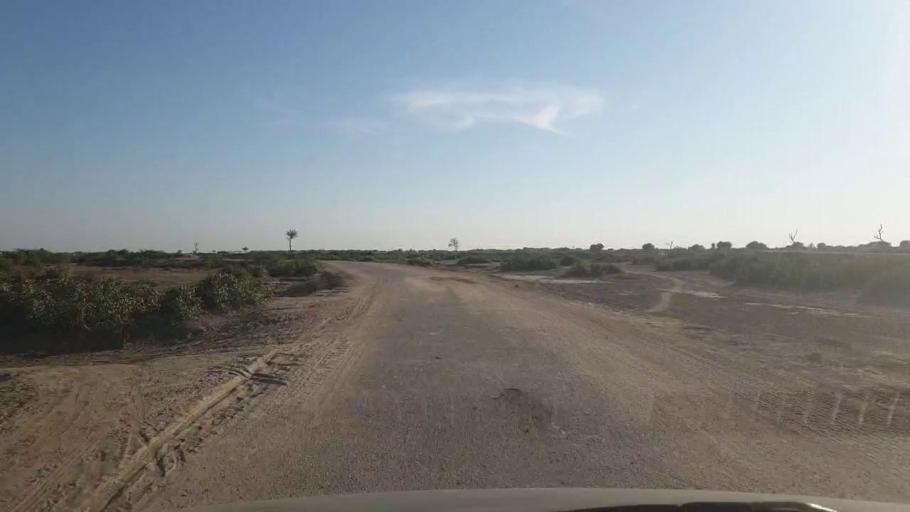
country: PK
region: Sindh
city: Dhoro Naro
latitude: 25.4292
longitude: 69.5330
